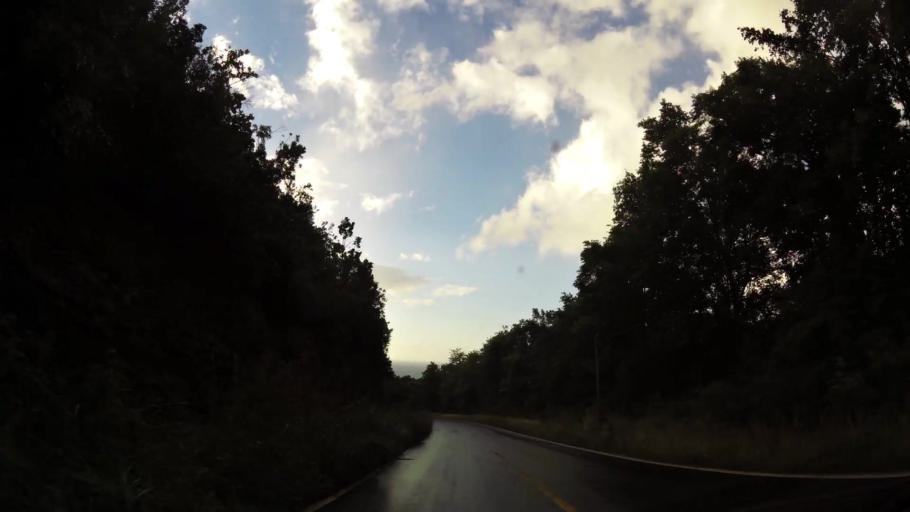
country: DM
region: Saint Peter
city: Colihaut
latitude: 15.5295
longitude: -61.4671
